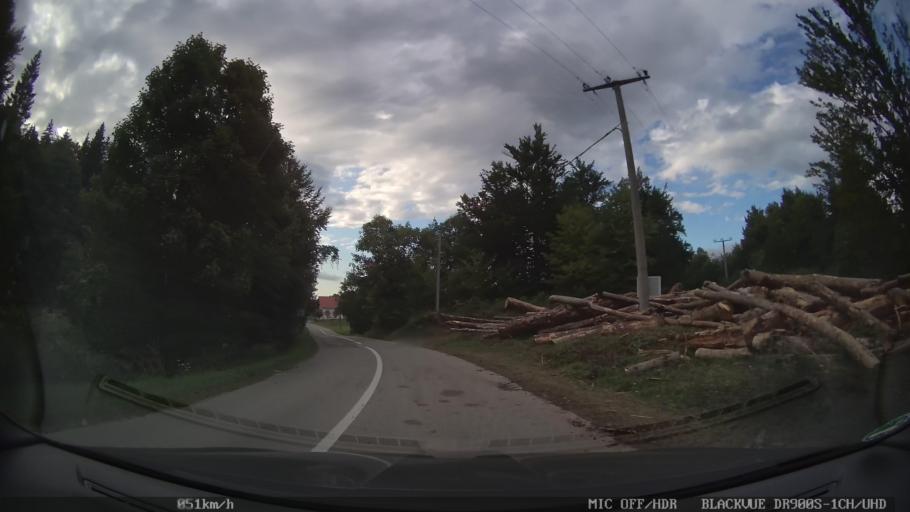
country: HR
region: Licko-Senjska
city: Jezerce
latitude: 44.9625
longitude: 15.5268
